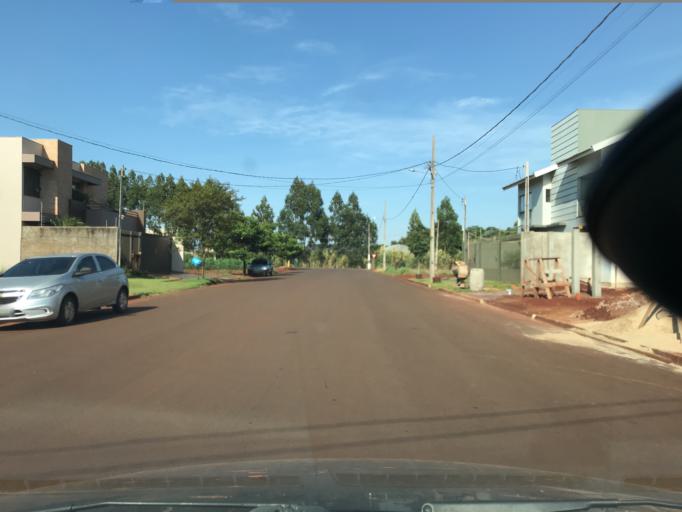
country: BR
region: Parana
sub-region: Palotina
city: Palotina
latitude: -24.2931
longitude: -53.8393
